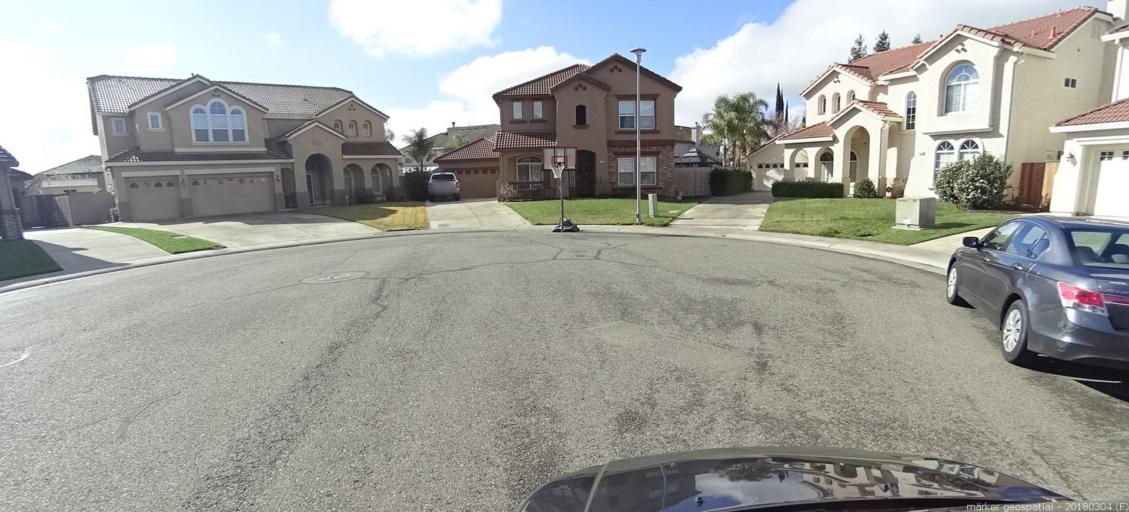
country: US
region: California
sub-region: Sacramento County
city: Vineyard
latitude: 38.4581
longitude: -121.3189
